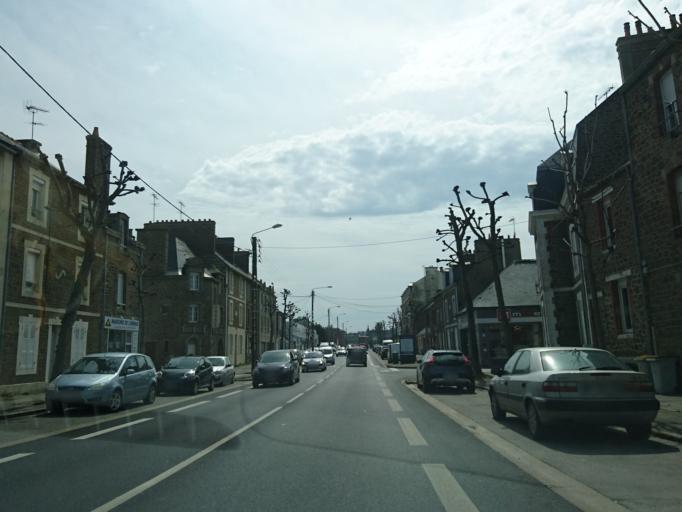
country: FR
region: Brittany
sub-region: Departement d'Ille-et-Vilaine
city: Saint-Malo
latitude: 48.6433
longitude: -2.0086
